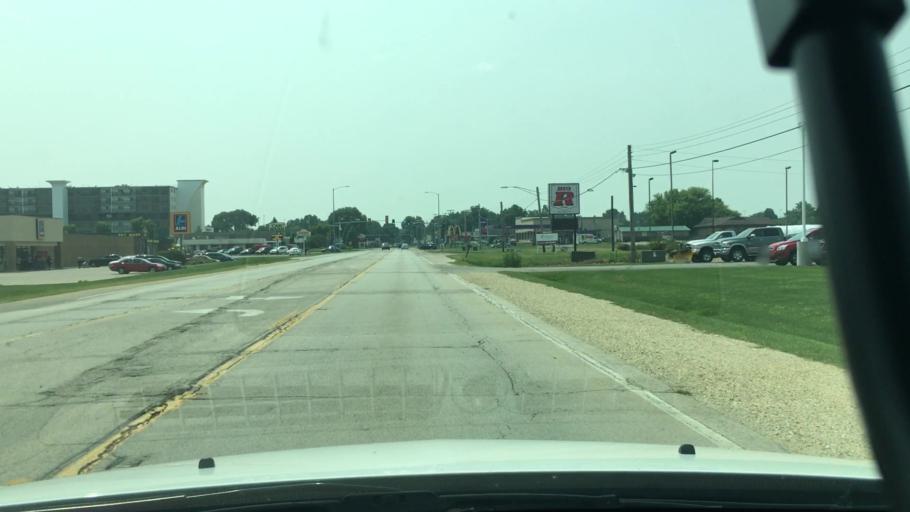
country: US
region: Illinois
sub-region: Ogle County
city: Hillcrest
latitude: 41.9381
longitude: -89.0682
